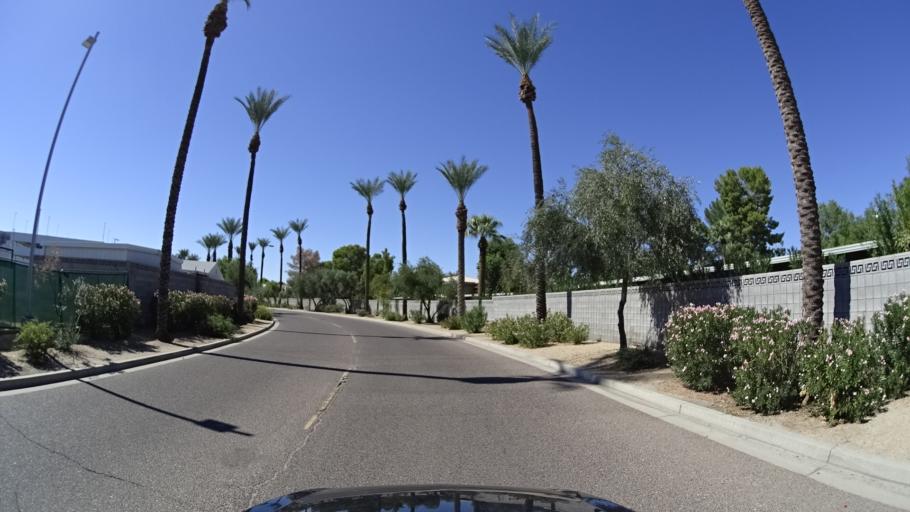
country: US
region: Arizona
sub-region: Maricopa County
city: Phoenix
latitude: 33.5119
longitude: -112.0261
